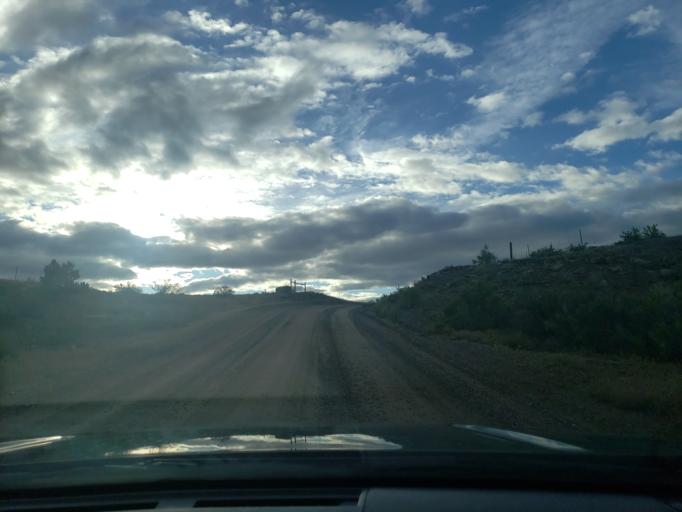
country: US
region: Colorado
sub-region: Mesa County
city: Fruita
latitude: 39.1425
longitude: -108.7580
